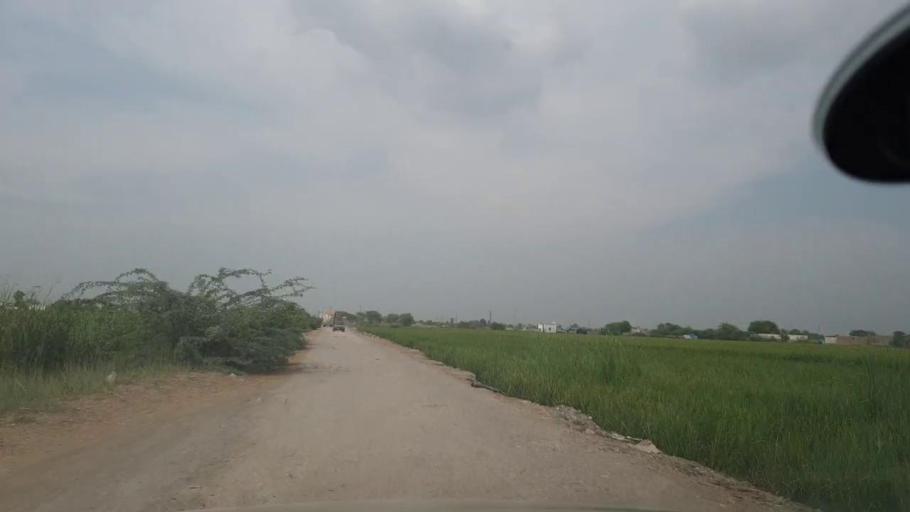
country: PK
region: Sindh
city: Jacobabad
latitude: 28.2547
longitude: 68.4370
